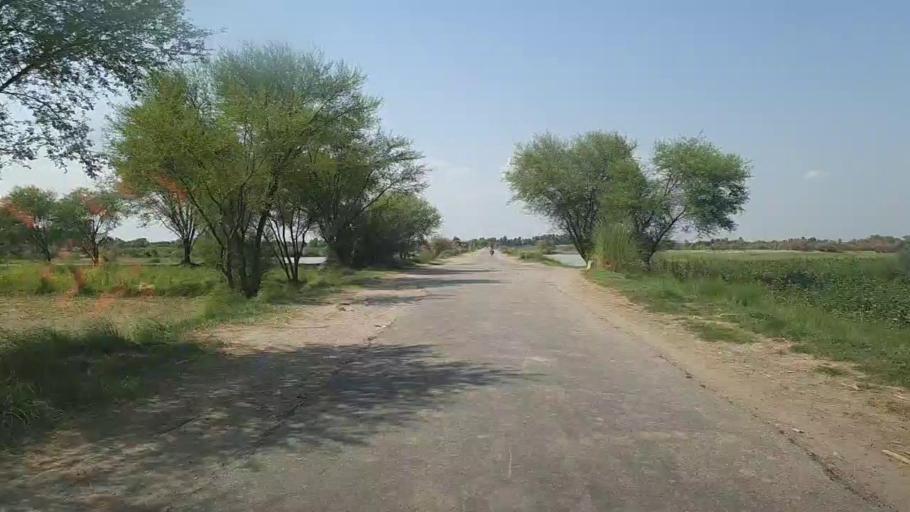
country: PK
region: Sindh
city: Khairpur
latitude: 28.0756
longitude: 69.6390
